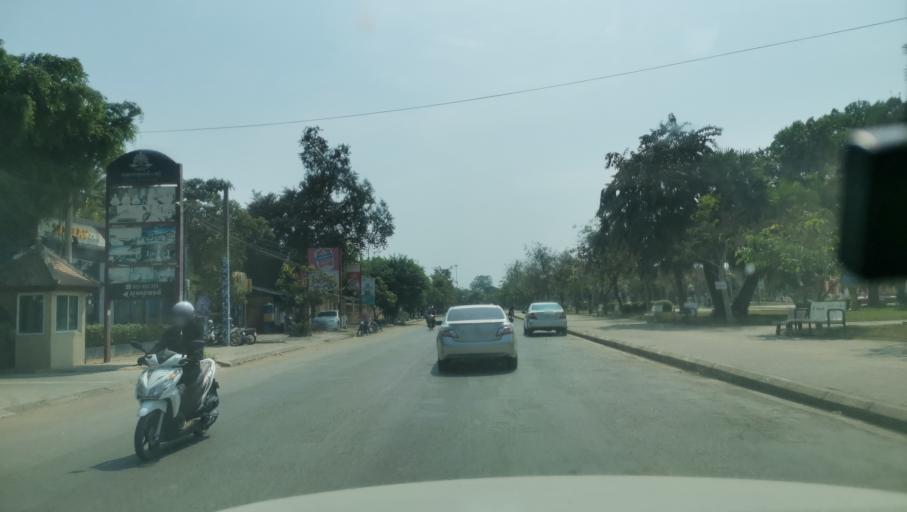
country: KH
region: Battambang
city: Battambang
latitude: 13.0968
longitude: 103.2002
